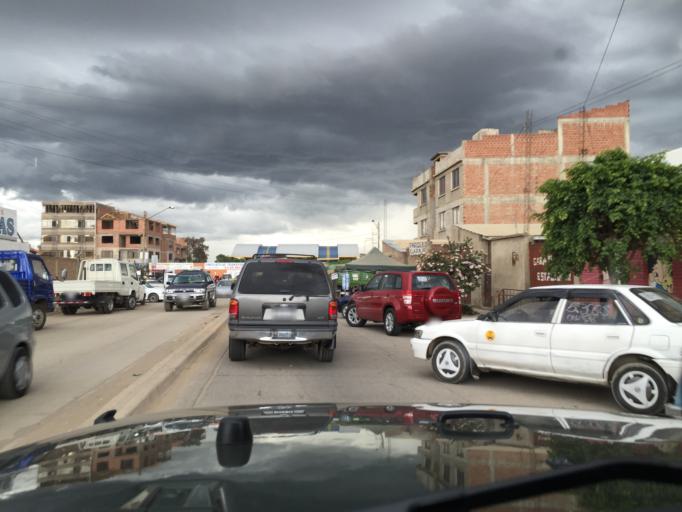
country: BO
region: Cochabamba
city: Cochabamba
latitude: -17.4009
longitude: -66.1859
